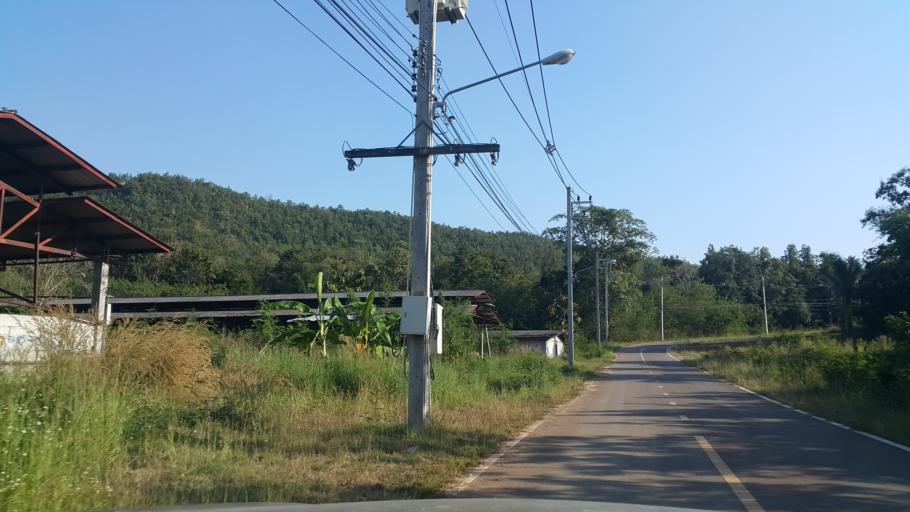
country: TH
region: Lamphun
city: Mae Tha
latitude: 18.5134
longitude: 99.1154
